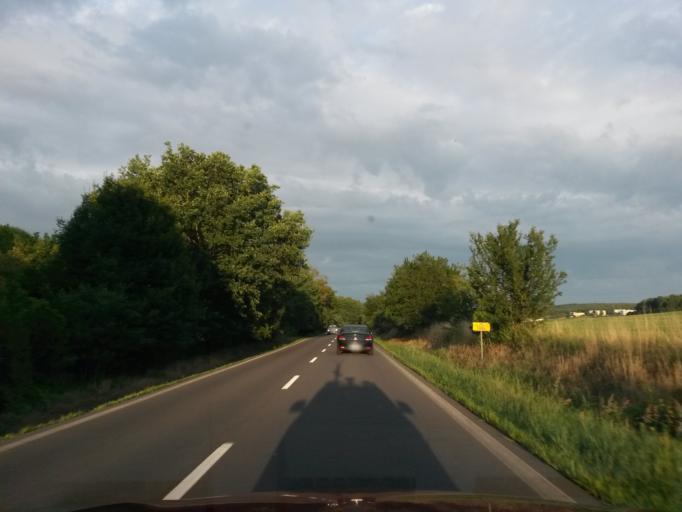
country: SK
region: Banskobystricky
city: Lucenec
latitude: 48.3465
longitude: 19.5967
